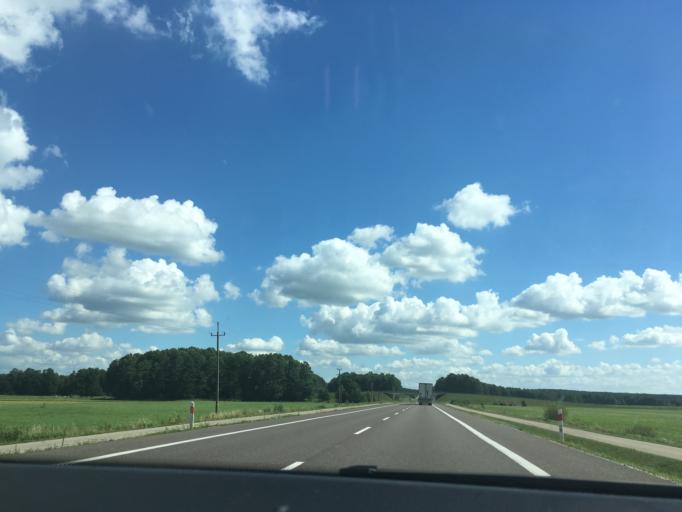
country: PL
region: Podlasie
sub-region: Powiat augustowski
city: Augustow
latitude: 53.7545
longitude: 23.0880
